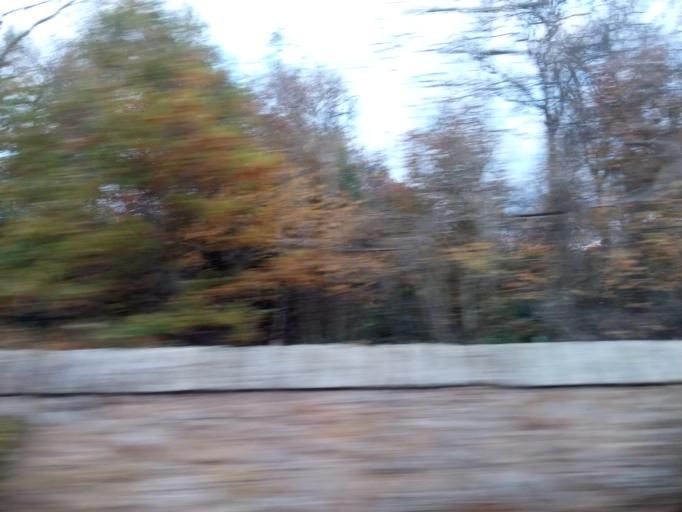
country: GB
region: Scotland
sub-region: Fife
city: Pathhead
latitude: 55.8738
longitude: -2.9984
